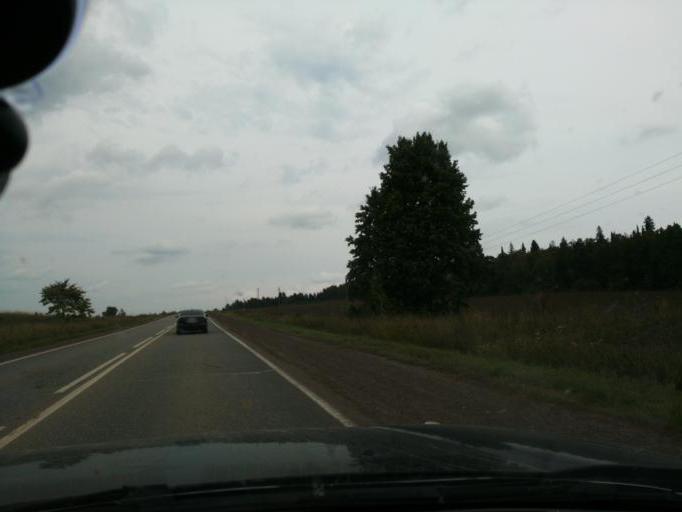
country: RU
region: Perm
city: Kuyeda
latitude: 56.4668
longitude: 55.6734
